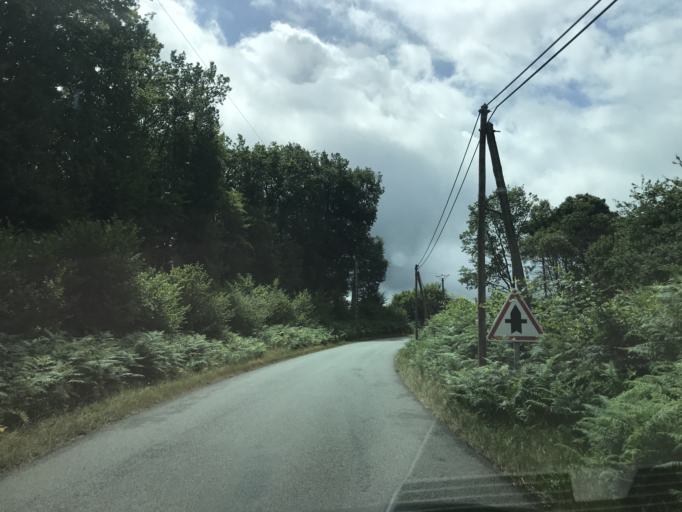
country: FR
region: Auvergne
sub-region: Departement du Cantal
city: Pleaux
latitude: 45.2672
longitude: 2.2064
